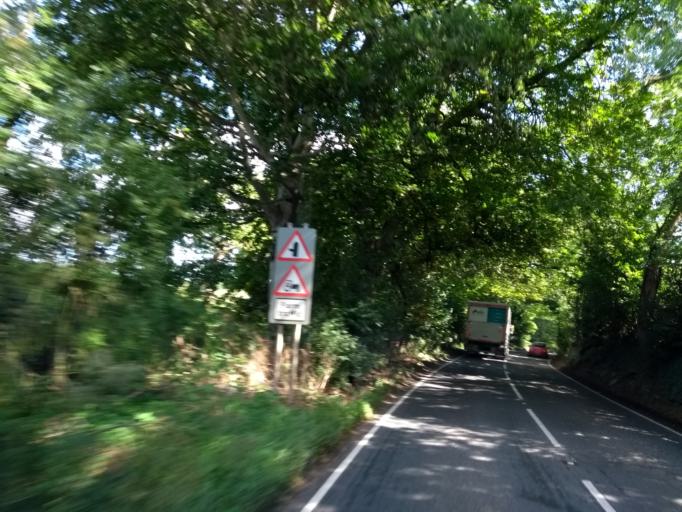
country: GB
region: England
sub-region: Somerset
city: Street
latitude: 51.0697
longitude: -2.7271
